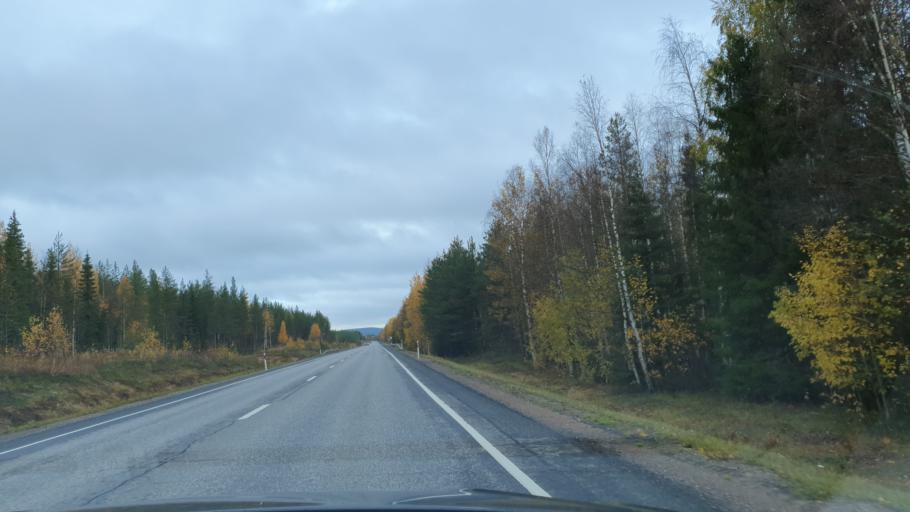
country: FI
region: Lapland
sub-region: Rovaniemi
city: Rovaniemi
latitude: 66.5584
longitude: 25.6463
